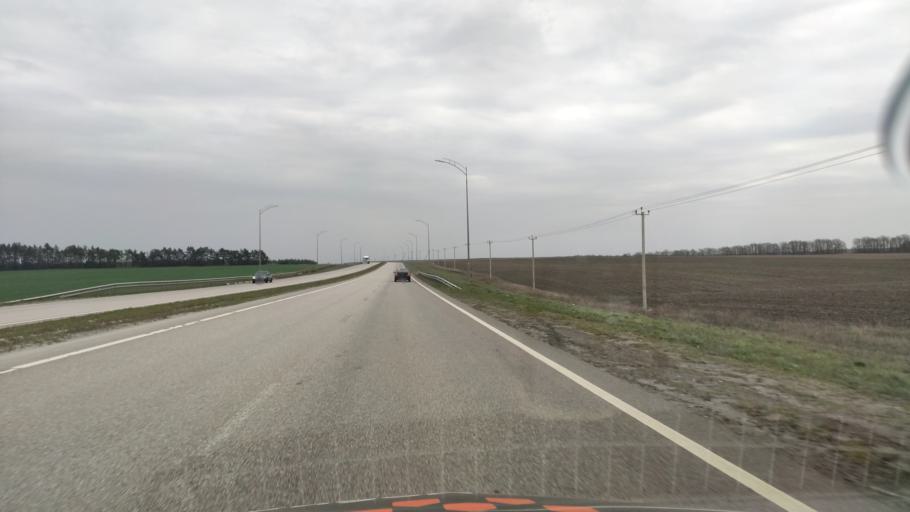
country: RU
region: Belgorod
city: Staryy Oskol
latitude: 51.3913
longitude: 37.8667
